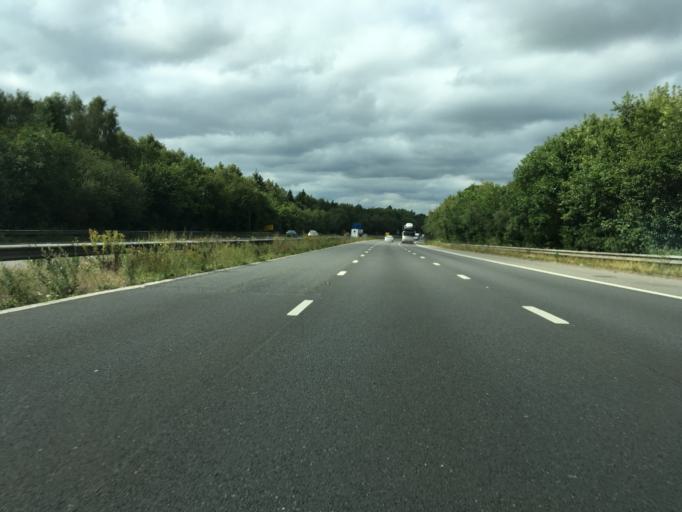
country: GB
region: England
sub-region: West Sussex
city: Maidenbower
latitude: 51.1209
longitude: -0.1392
